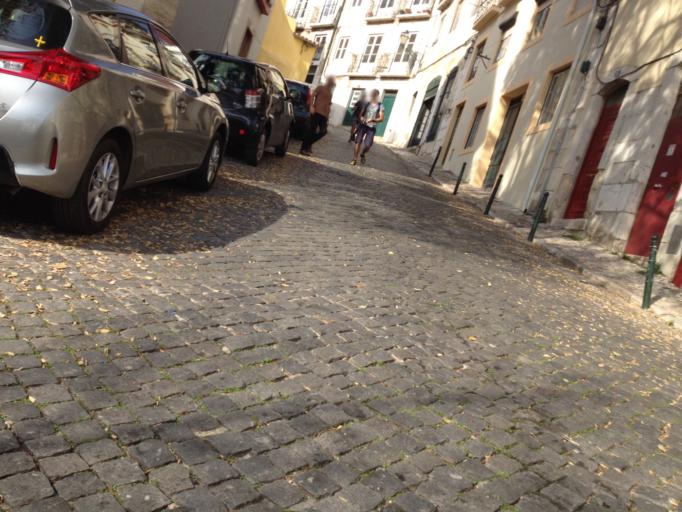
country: PT
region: Lisbon
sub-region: Lisbon
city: Lisbon
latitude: 38.7093
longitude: -9.1481
